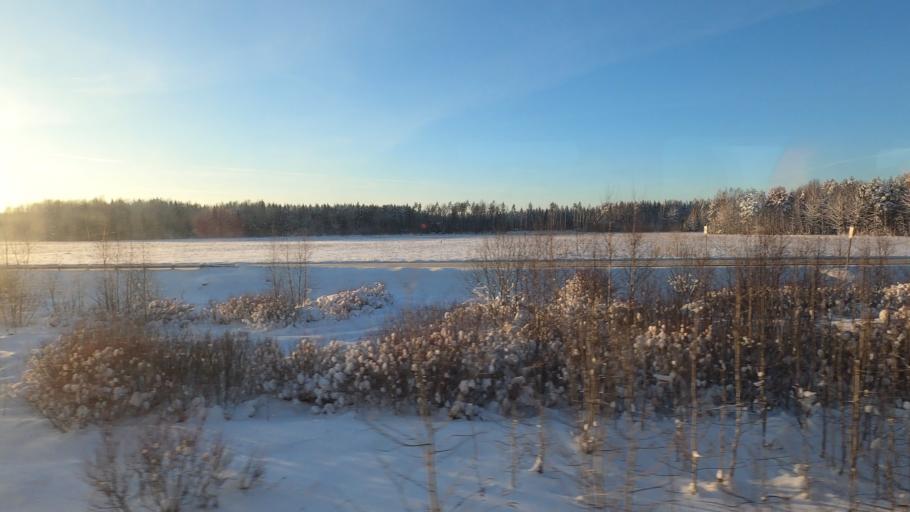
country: RU
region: Moskovskaya
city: Novo-Nikol'skoye
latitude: 56.6490
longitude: 37.5644
